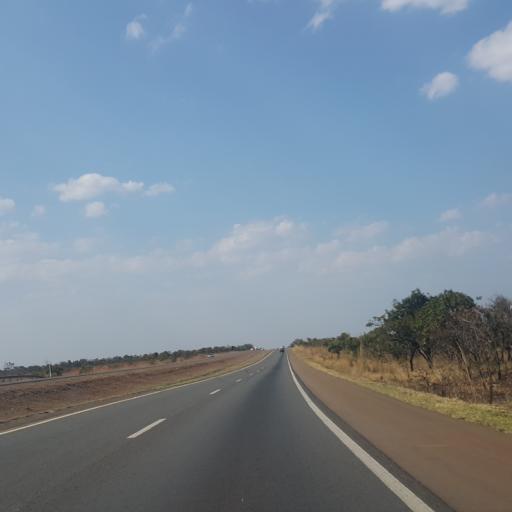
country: BR
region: Goias
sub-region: Abadiania
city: Abadiania
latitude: -16.2025
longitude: -48.7385
